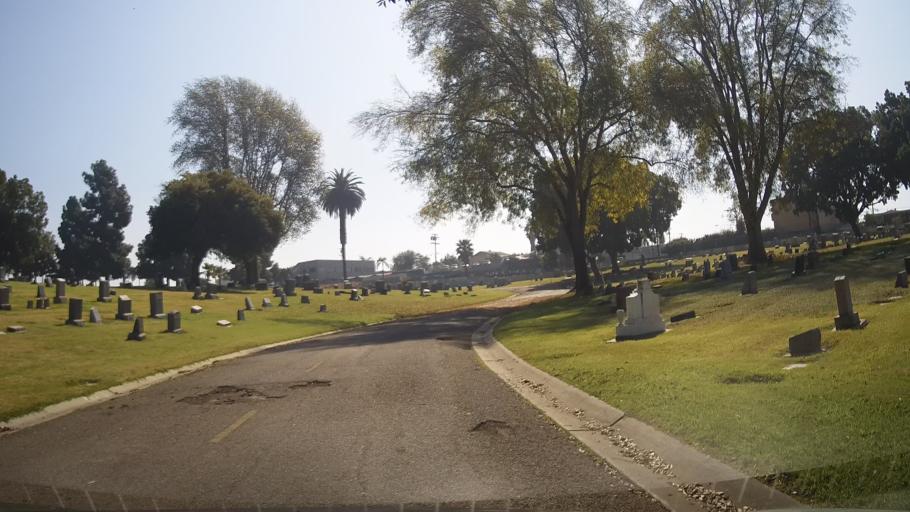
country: US
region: California
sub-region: San Diego County
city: National City
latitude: 32.7059
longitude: -117.1133
